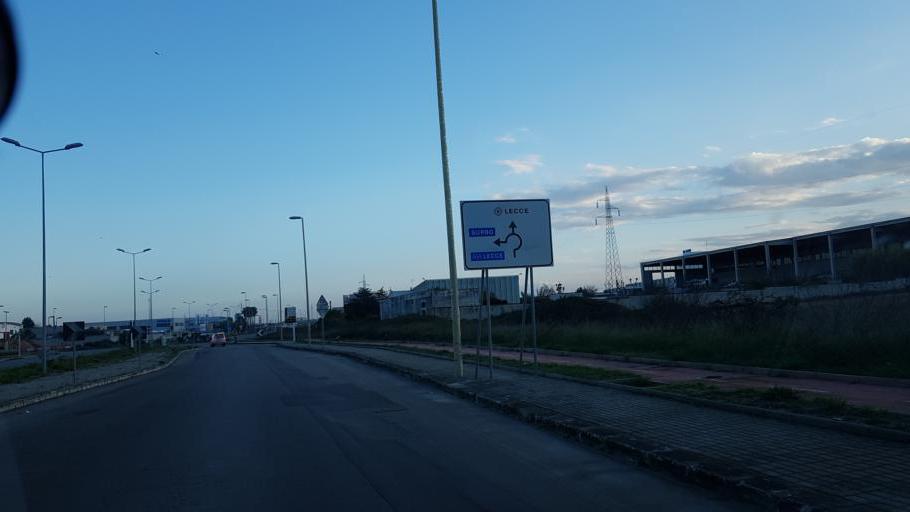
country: IT
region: Apulia
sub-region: Provincia di Lecce
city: Giorgilorio
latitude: 40.3749
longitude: 18.1344
